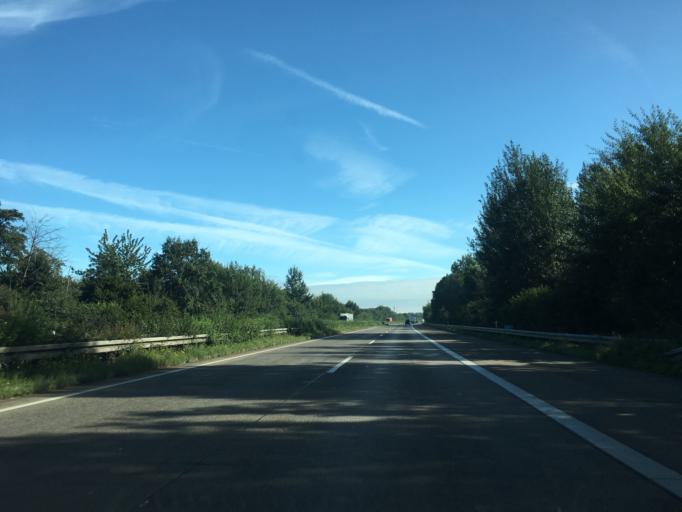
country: DE
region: North Rhine-Westphalia
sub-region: Regierungsbezirk Munster
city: Ladbergen
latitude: 52.1607
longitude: 7.7472
